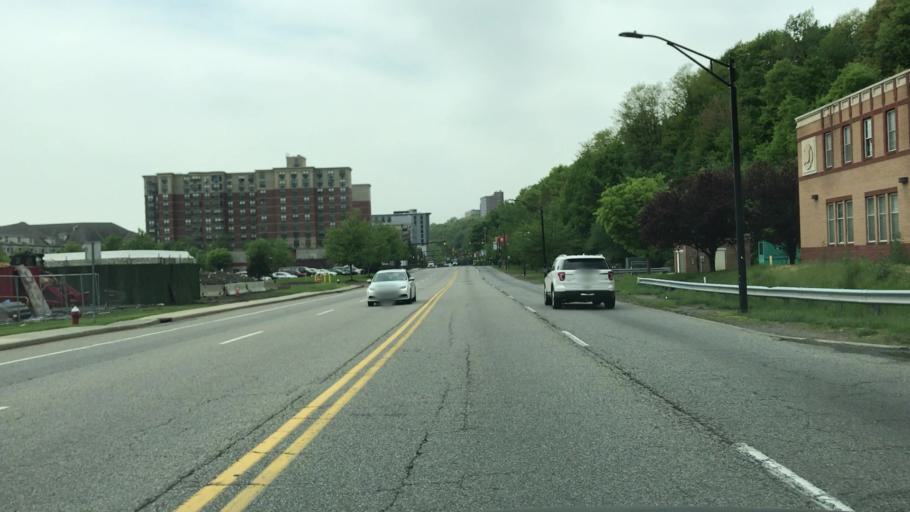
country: US
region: New Jersey
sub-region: Hudson County
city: West New York
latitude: 40.7822
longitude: -74.0087
